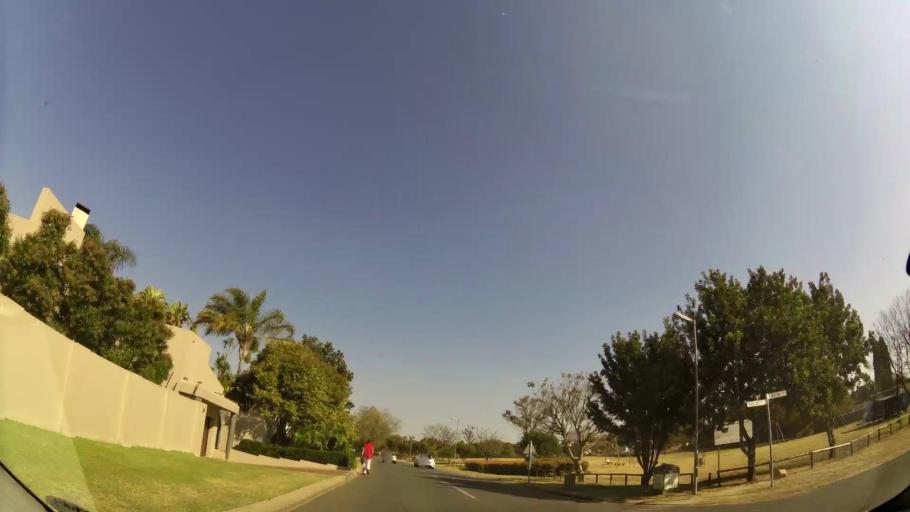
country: ZA
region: Gauteng
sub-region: City of Johannesburg Metropolitan Municipality
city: Johannesburg
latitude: -26.0899
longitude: 28.0184
